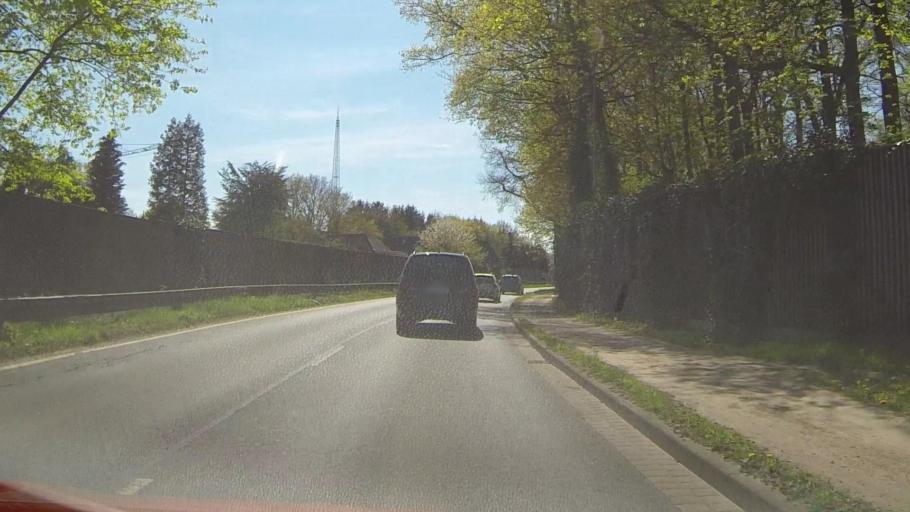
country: DE
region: Schleswig-Holstein
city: Tornesch
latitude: 53.6913
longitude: 9.6992
